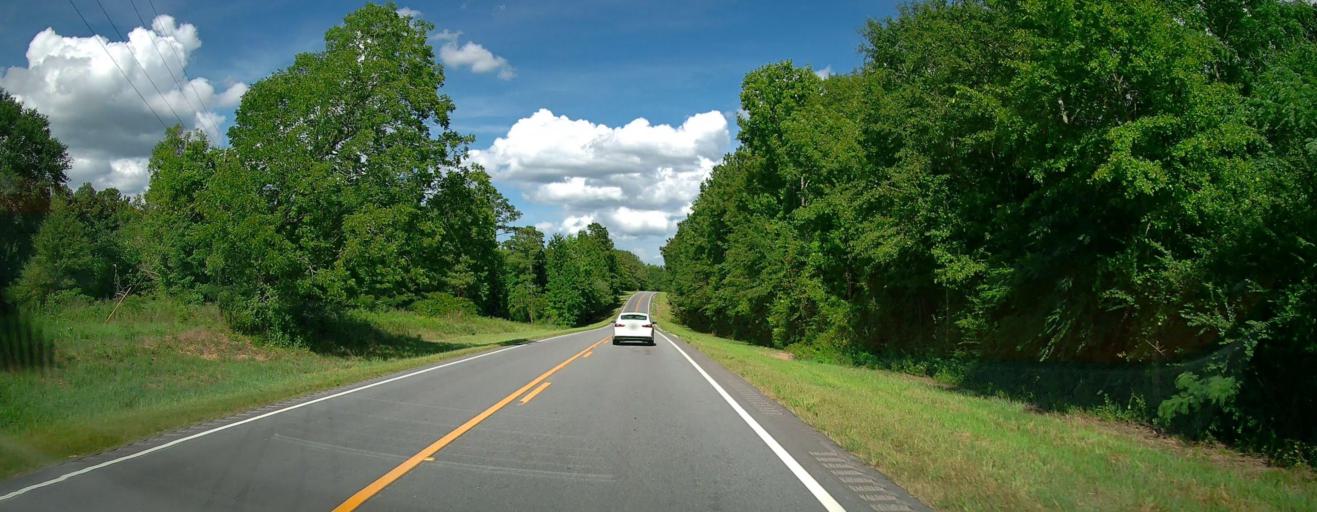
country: US
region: Alabama
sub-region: Lee County
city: Auburn
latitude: 32.4331
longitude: -85.4212
